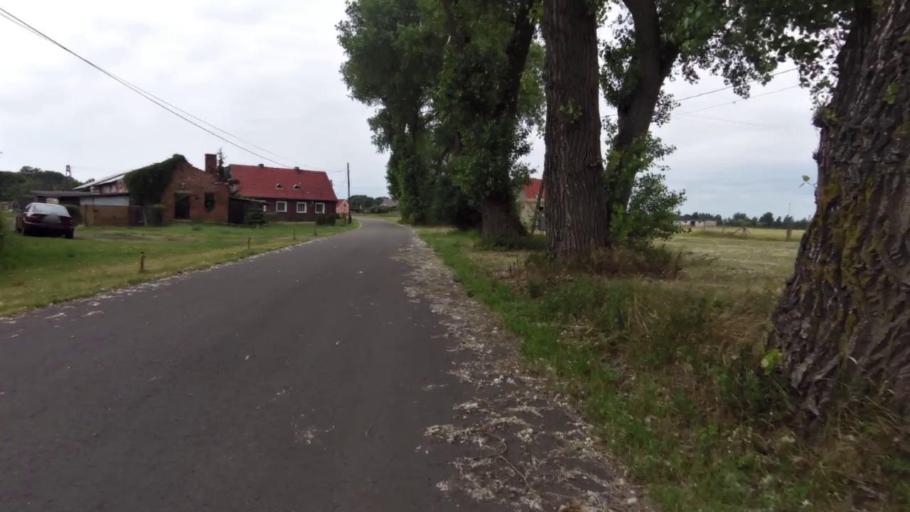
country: PL
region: West Pomeranian Voivodeship
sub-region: Powiat goleniowski
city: Stepnica
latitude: 53.7189
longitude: 14.5615
